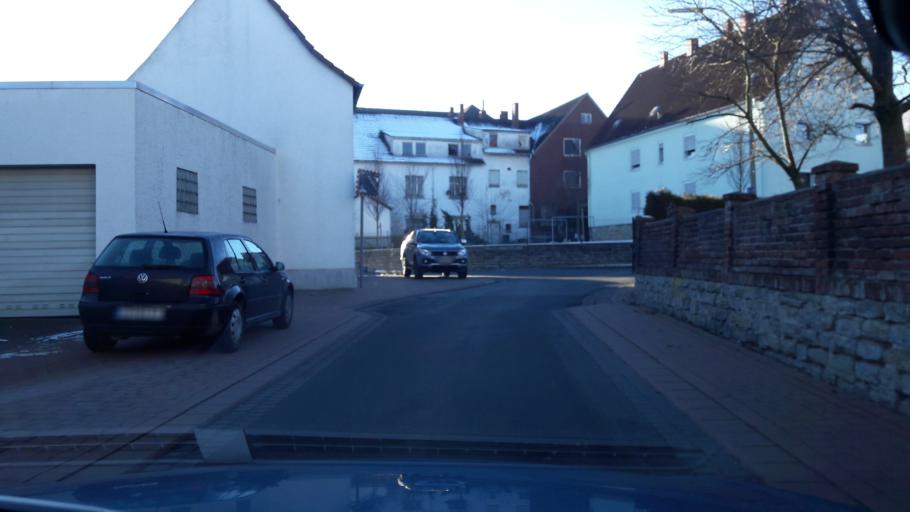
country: DE
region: North Rhine-Westphalia
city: Erwitte
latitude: 51.6139
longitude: 8.3359
